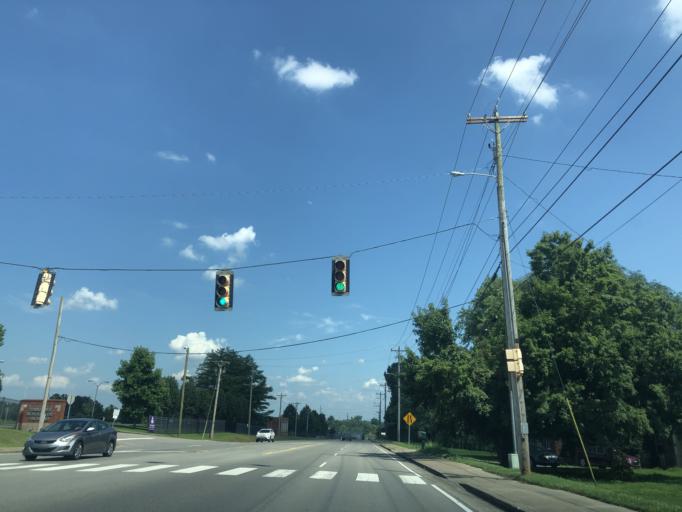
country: US
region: Tennessee
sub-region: Davidson County
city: Lakewood
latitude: 36.1667
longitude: -86.6551
